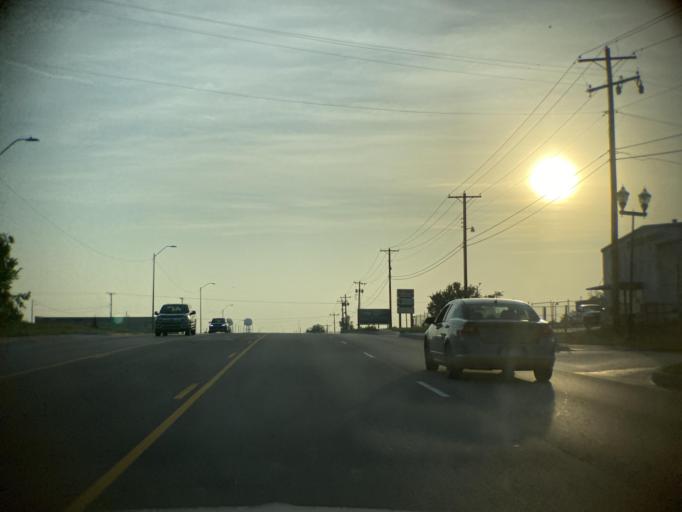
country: US
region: Oklahoma
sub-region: Oklahoma County
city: Midwest City
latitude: 35.4353
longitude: -97.3727
